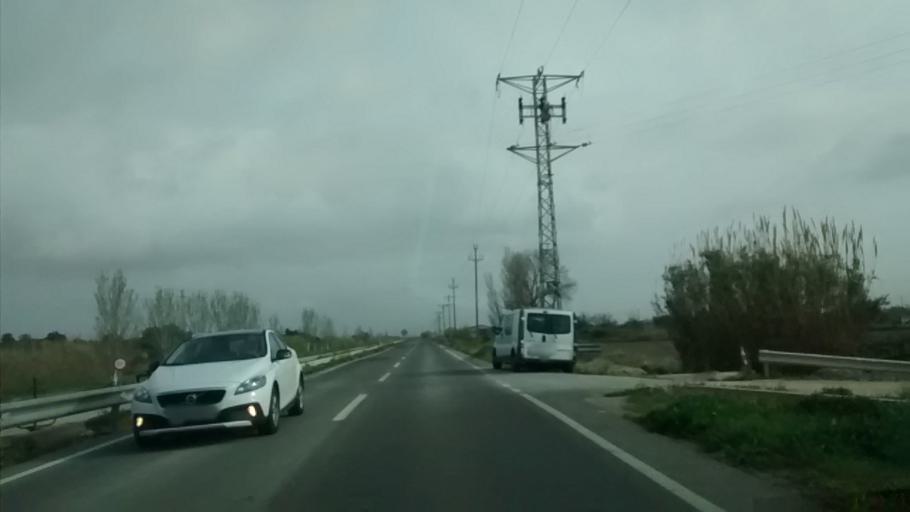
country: ES
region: Catalonia
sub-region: Provincia de Tarragona
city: Sant Carles de la Rapita
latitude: 40.6265
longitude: 0.6002
